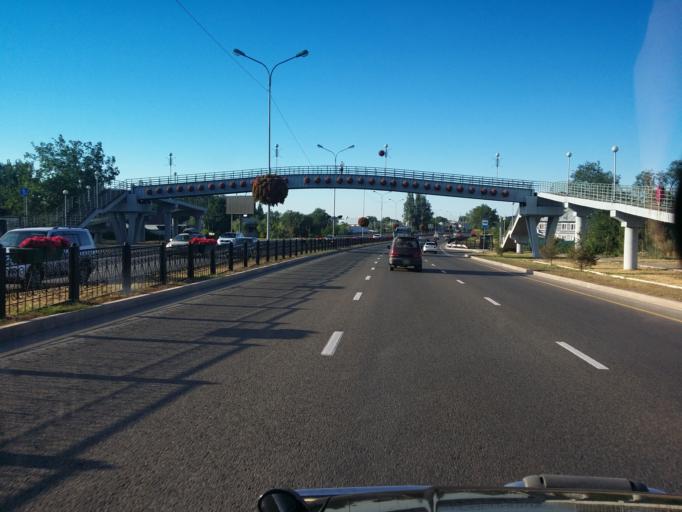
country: KZ
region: Almaty Qalasy
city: Almaty
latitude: 43.2757
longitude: 76.9843
